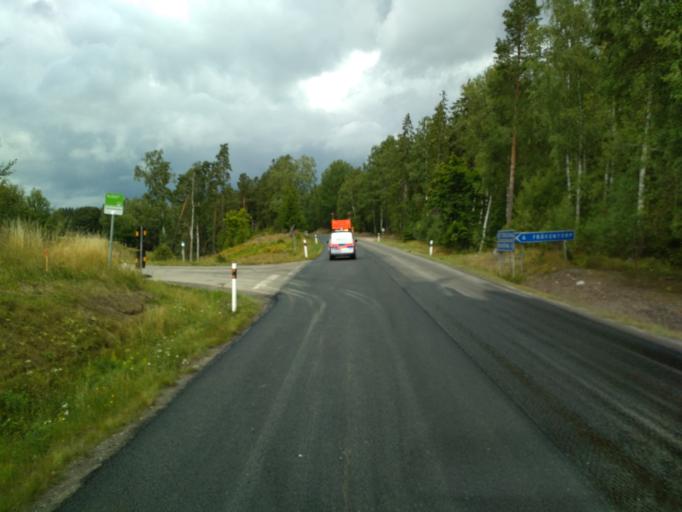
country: SE
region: Soedermanland
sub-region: Flens Kommun
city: Malmkoping
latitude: 59.1601
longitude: 16.6858
